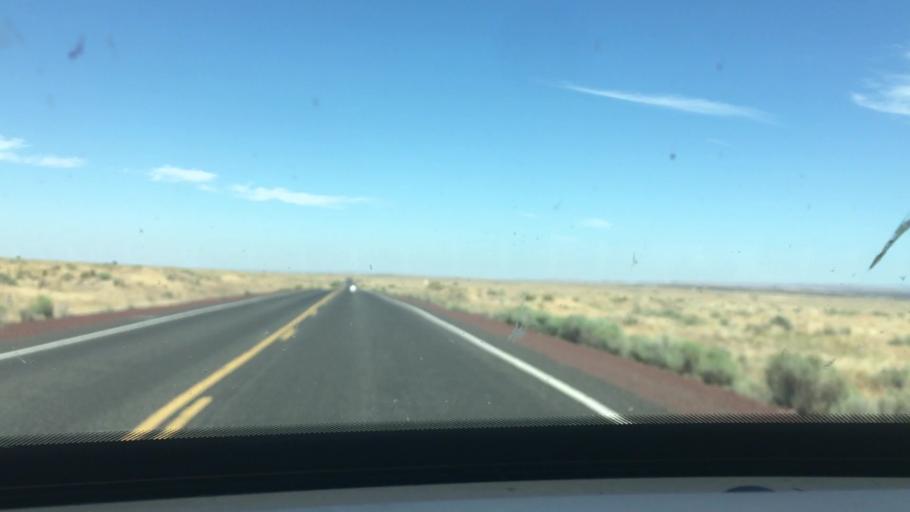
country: US
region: Oregon
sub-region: Jefferson County
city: Madras
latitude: 44.9901
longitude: -120.8344
